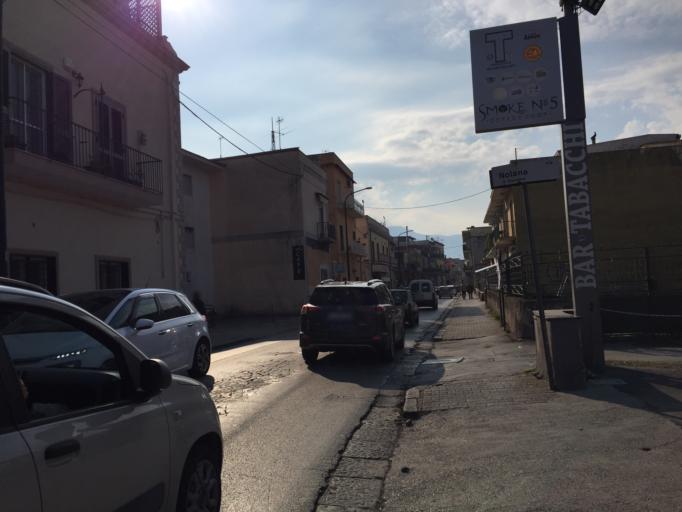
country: IT
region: Campania
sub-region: Provincia di Napoli
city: Pompei
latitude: 40.7532
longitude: 14.4992
